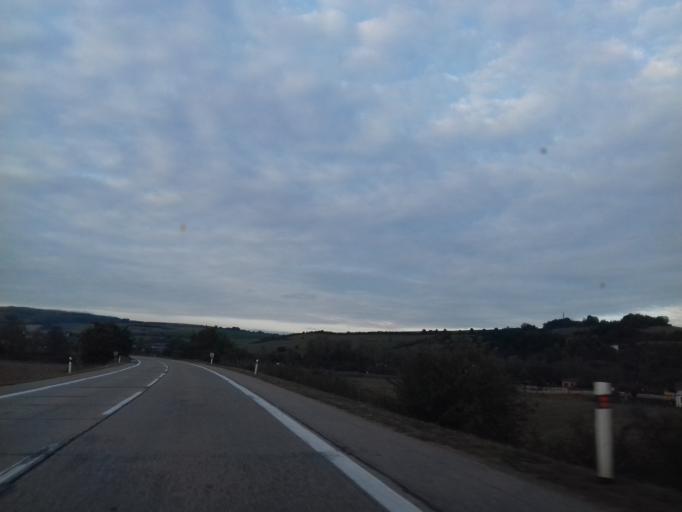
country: SK
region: Trenciansky
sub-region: Okres Trencin
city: Trencin
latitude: 48.8789
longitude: 17.9620
